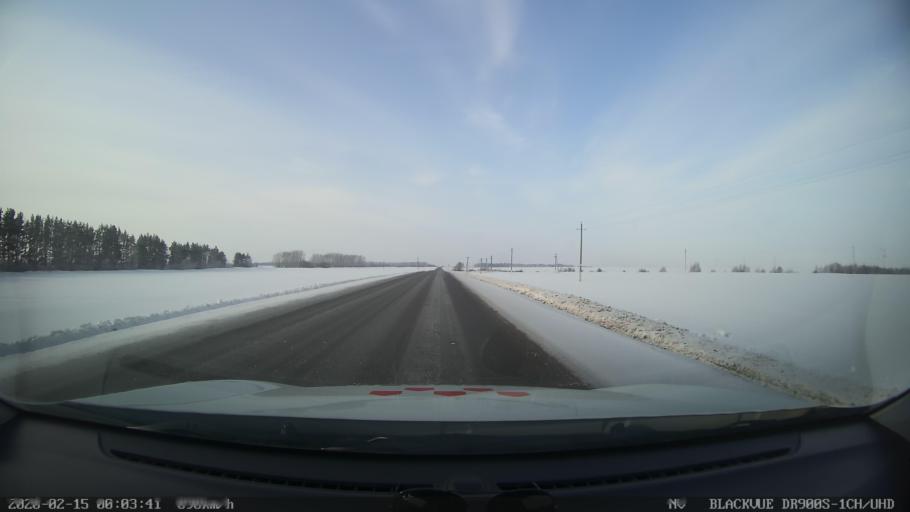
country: RU
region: Tatarstan
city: Kuybyshevskiy Zaton
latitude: 55.3743
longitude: 48.9940
